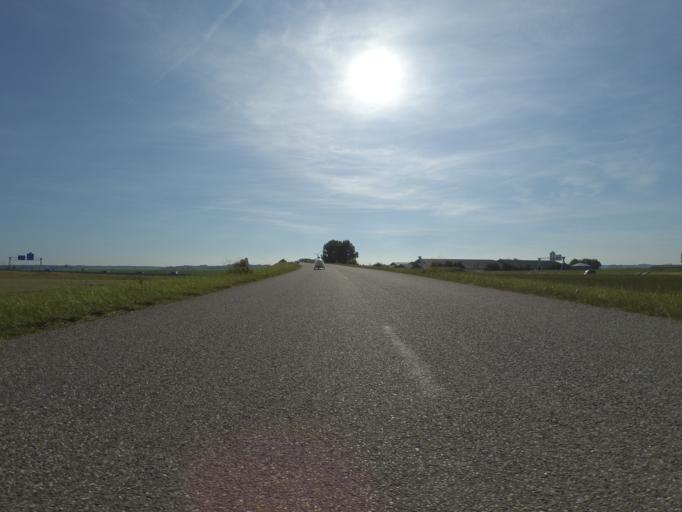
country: NL
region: North Brabant
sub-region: Gemeente Woensdrecht
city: Woensdrecht
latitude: 51.4251
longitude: 4.2747
